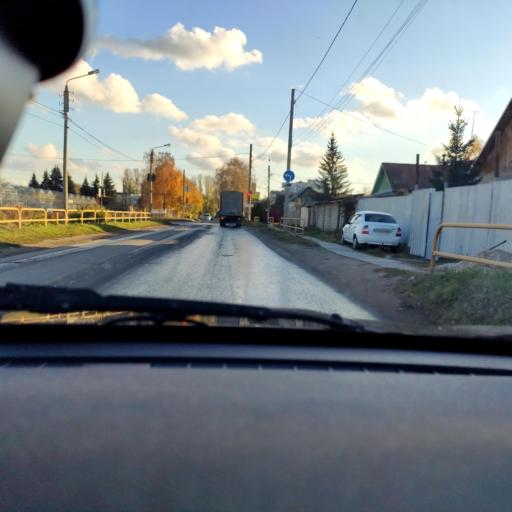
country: RU
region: Samara
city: Tol'yatti
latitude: 53.5357
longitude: 49.4285
